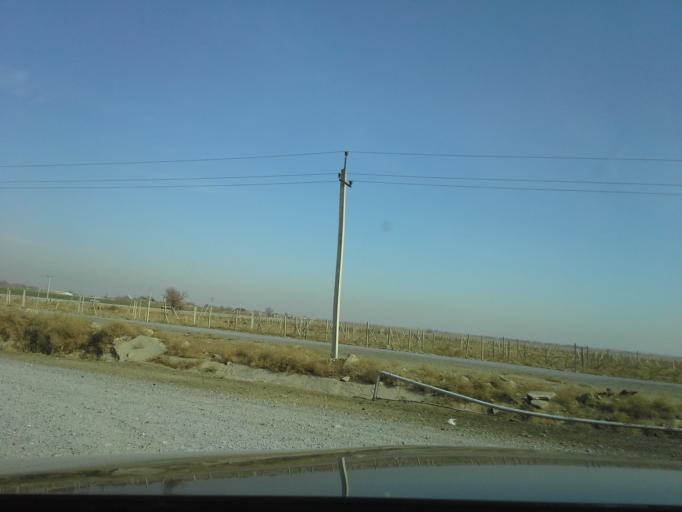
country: TM
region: Ahal
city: Abadan
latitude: 38.1082
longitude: 57.9838
